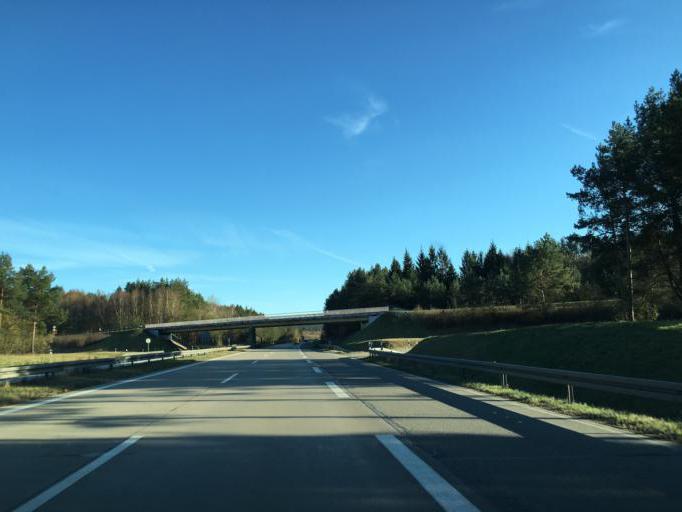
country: DE
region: Mecklenburg-Vorpommern
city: Lalendorf
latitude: 53.7744
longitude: 12.3202
